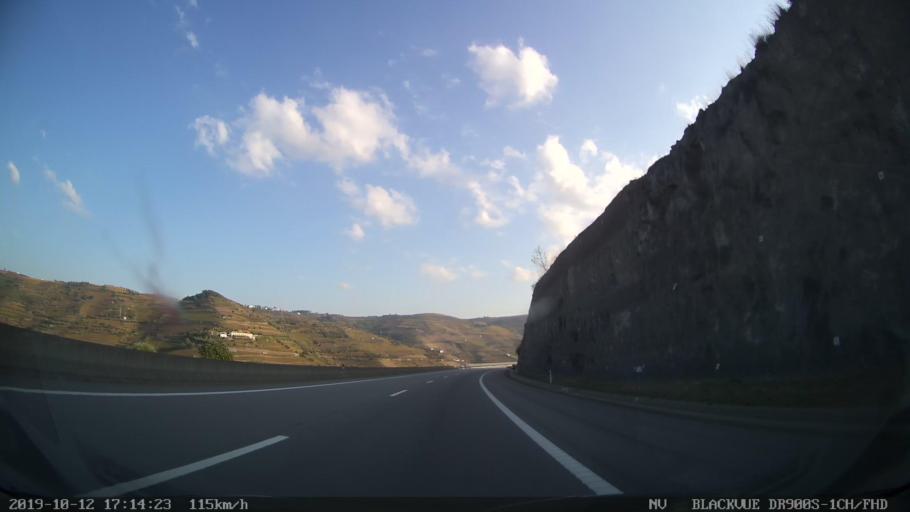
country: PT
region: Vila Real
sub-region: Peso da Regua
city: Peso da Regua
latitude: 41.1903
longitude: -7.7490
